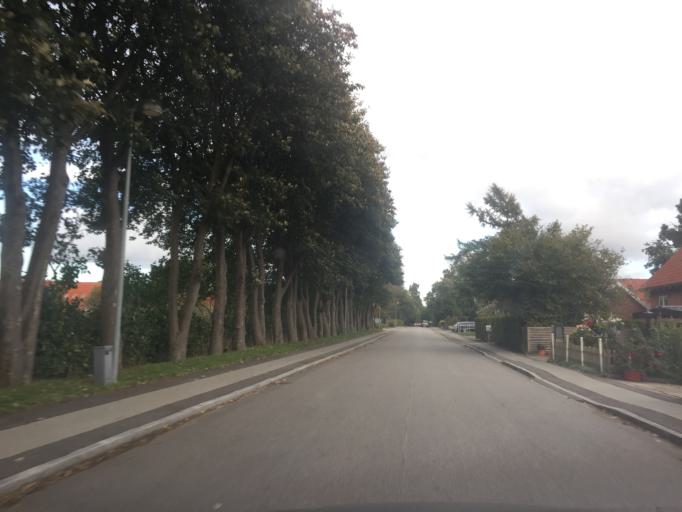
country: DK
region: Capital Region
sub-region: Hoje-Taastrup Kommune
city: Flong
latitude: 55.6614
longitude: 12.1762
